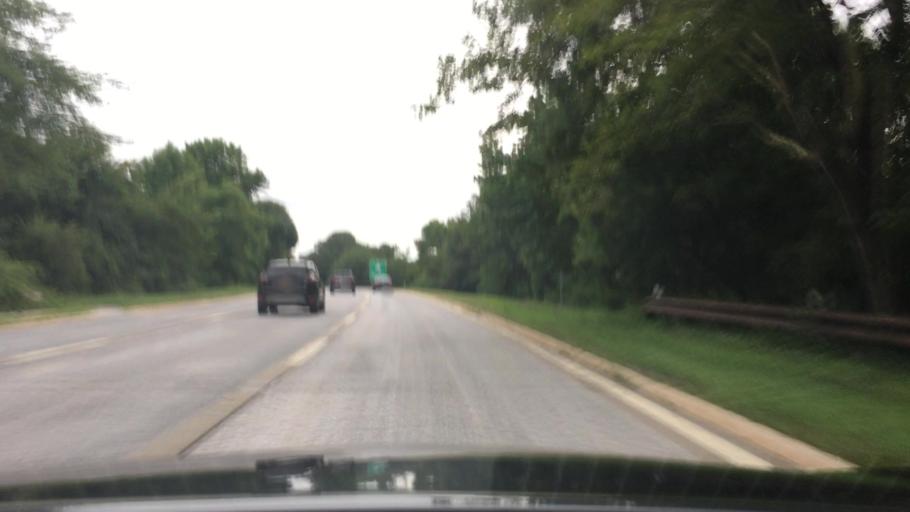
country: US
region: New York
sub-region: Nassau County
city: Wantagh
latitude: 40.6823
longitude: -73.5143
